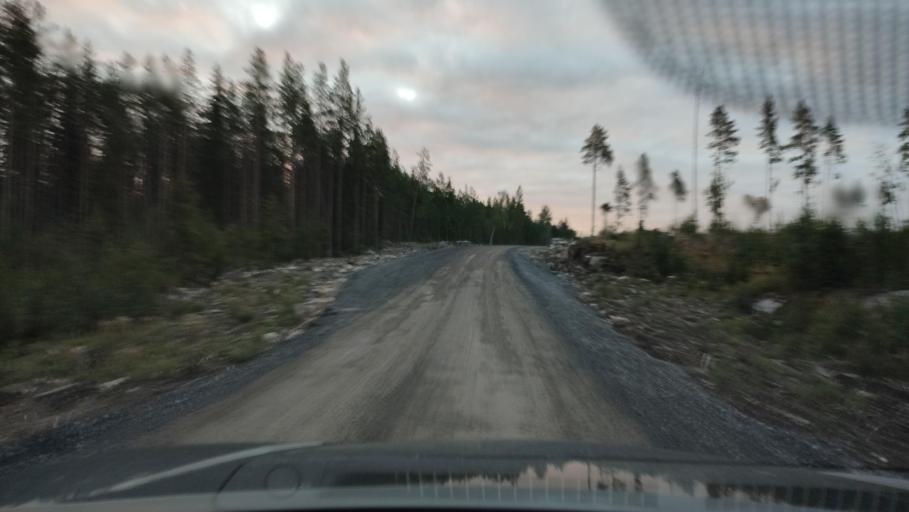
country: FI
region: Southern Ostrobothnia
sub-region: Suupohja
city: Karijoki
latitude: 62.1903
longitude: 21.5770
